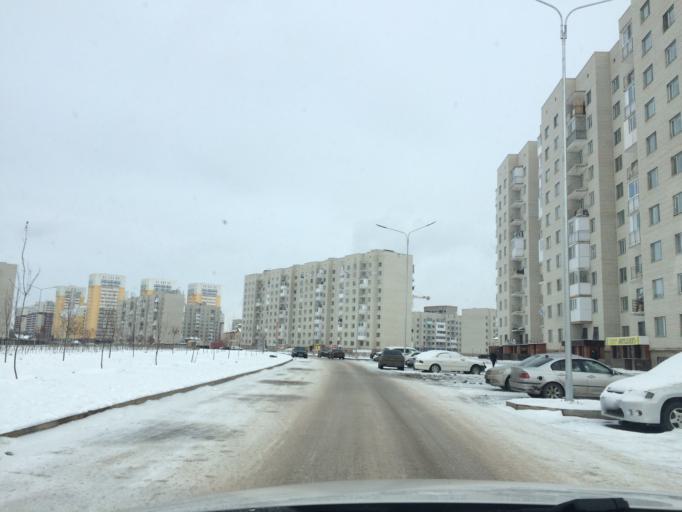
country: KZ
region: Astana Qalasy
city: Astana
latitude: 51.1238
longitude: 71.5050
